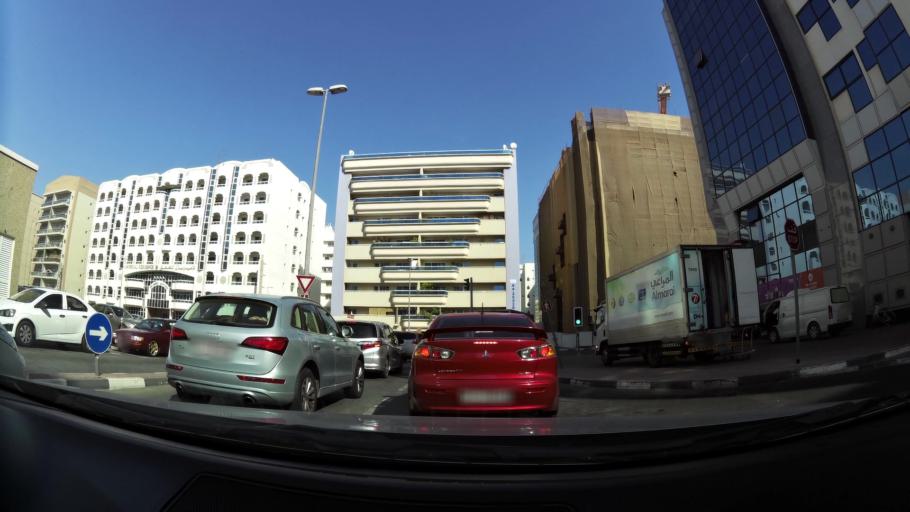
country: AE
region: Ash Shariqah
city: Sharjah
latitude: 25.2555
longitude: 55.3007
